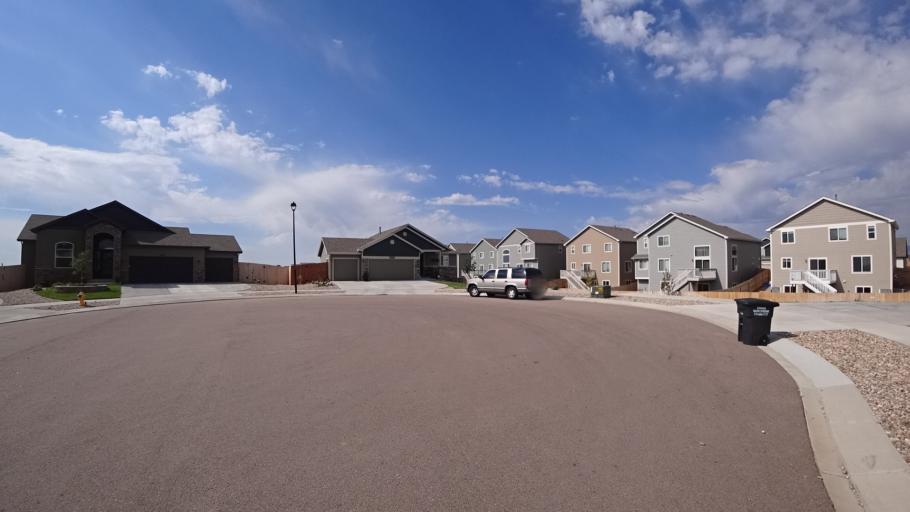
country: US
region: Colorado
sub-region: El Paso County
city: Cimarron Hills
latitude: 38.9186
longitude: -104.6810
